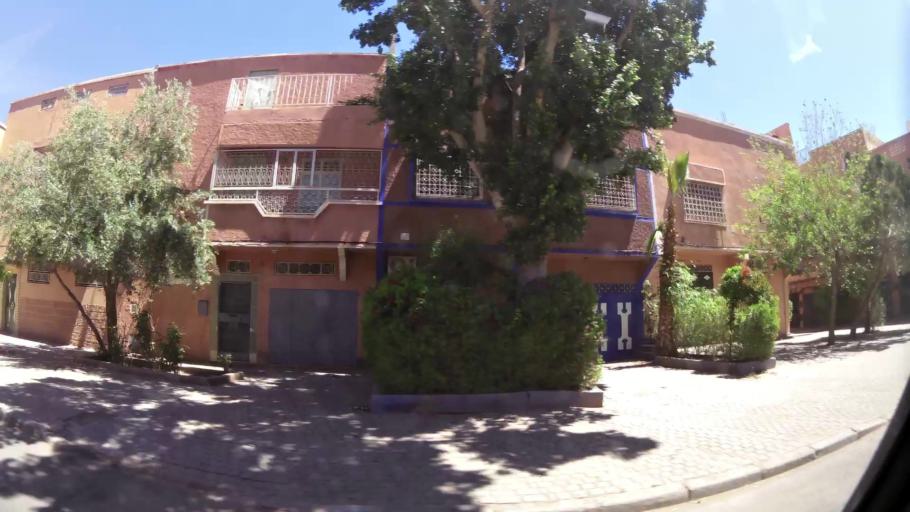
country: MA
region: Marrakech-Tensift-Al Haouz
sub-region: Marrakech
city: Marrakesh
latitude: 31.6484
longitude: -7.9974
